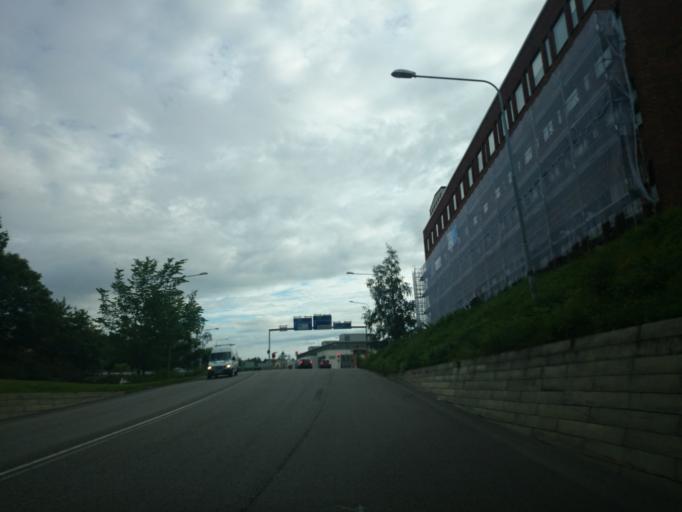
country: SE
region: Vaesternorrland
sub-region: Sundsvalls Kommun
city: Sundsvall
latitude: 62.3871
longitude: 17.3131
